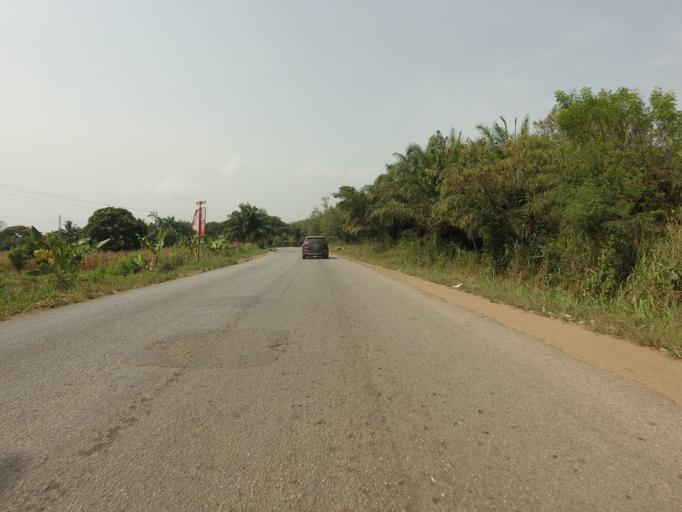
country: GH
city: Akropong
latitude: 6.2404
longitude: 0.1061
